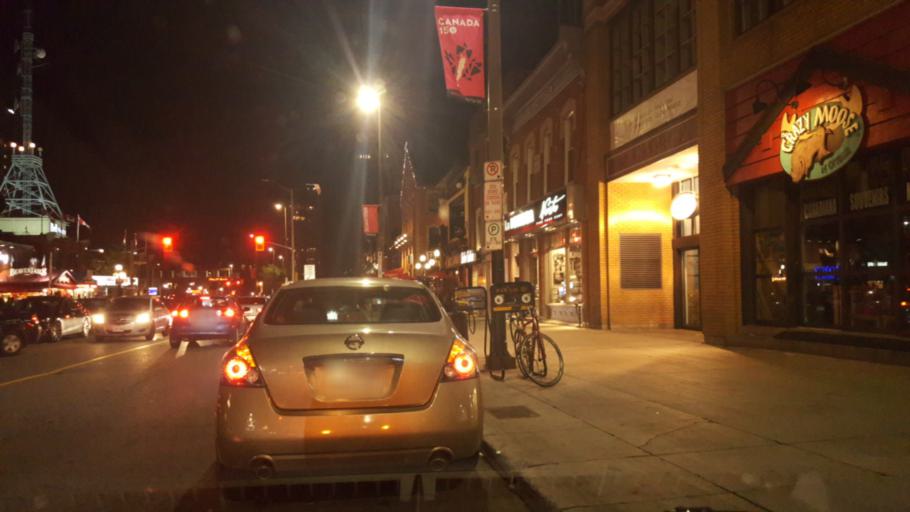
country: CA
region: Ontario
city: Ottawa
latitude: 45.4269
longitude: -75.6921
